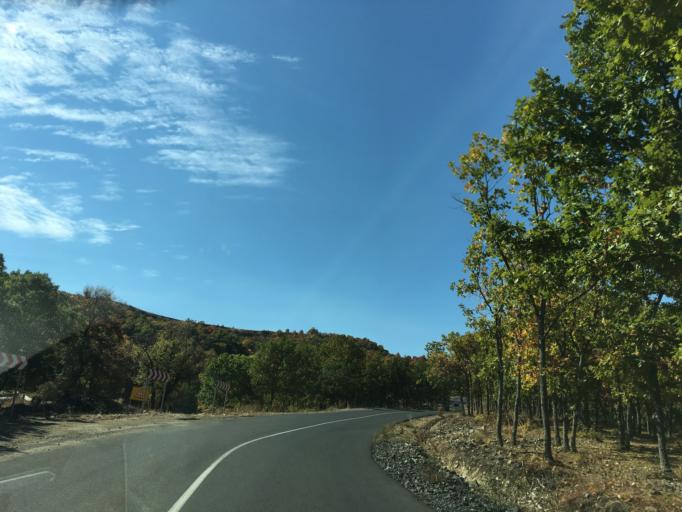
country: BG
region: Kurdzhali
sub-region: Obshtina Krumovgrad
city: Krumovgrad
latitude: 41.4752
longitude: 25.5471
